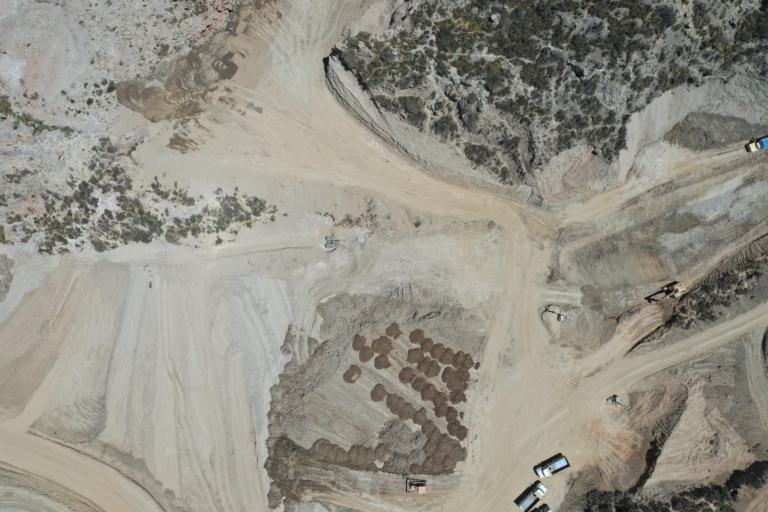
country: BO
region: La Paz
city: La Paz
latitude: -16.5571
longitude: -68.1303
